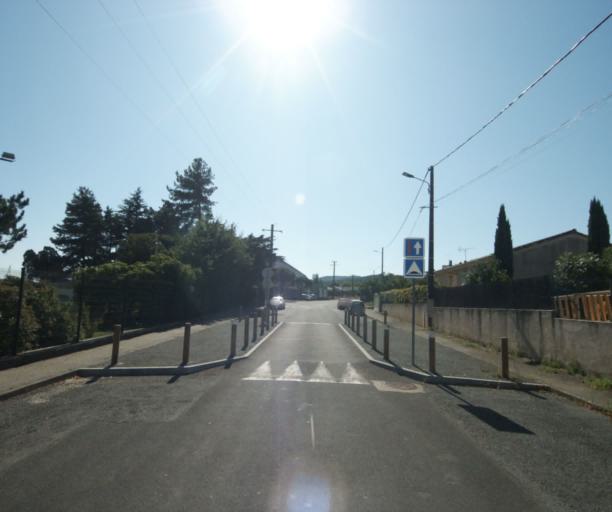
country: FR
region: Midi-Pyrenees
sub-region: Departement de la Haute-Garonne
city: Revel
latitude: 43.4518
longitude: 2.0149
